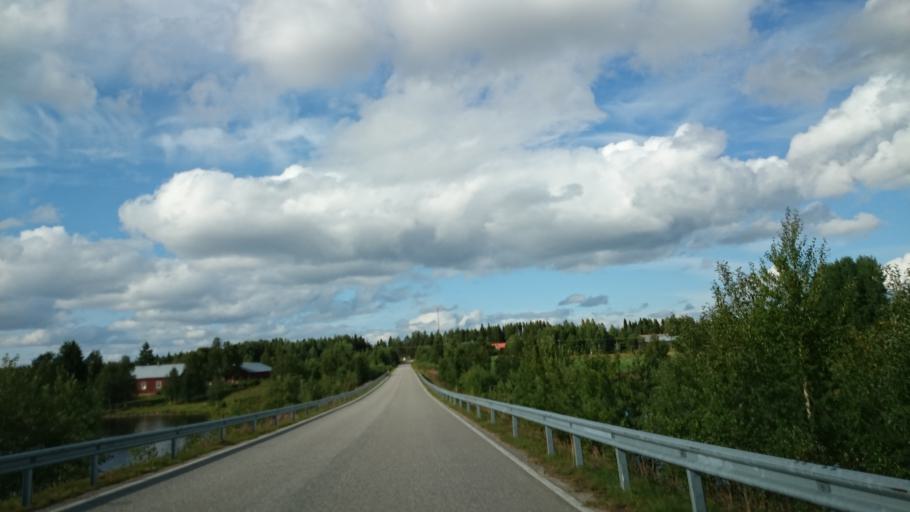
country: FI
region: Kainuu
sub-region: Kehys-Kainuu
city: Suomussalmi
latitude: 64.7427
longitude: 29.4396
